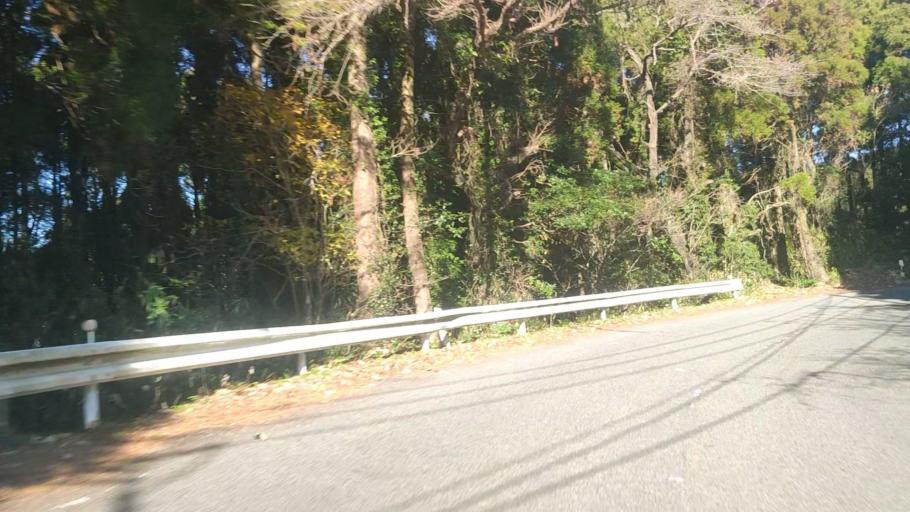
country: JP
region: Kagoshima
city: Kokubu-matsuki
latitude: 31.6695
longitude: 130.8281
